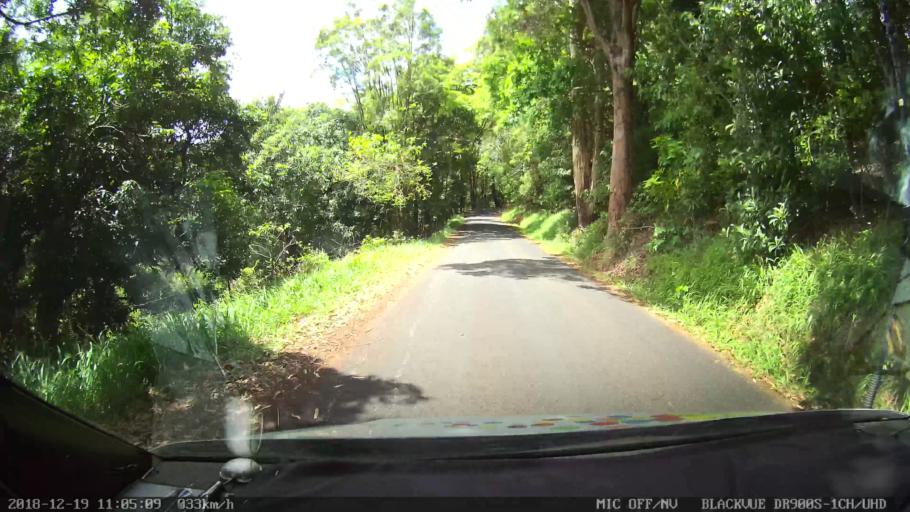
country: AU
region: New South Wales
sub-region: Lismore Municipality
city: Nimbin
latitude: -28.6158
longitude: 153.2650
